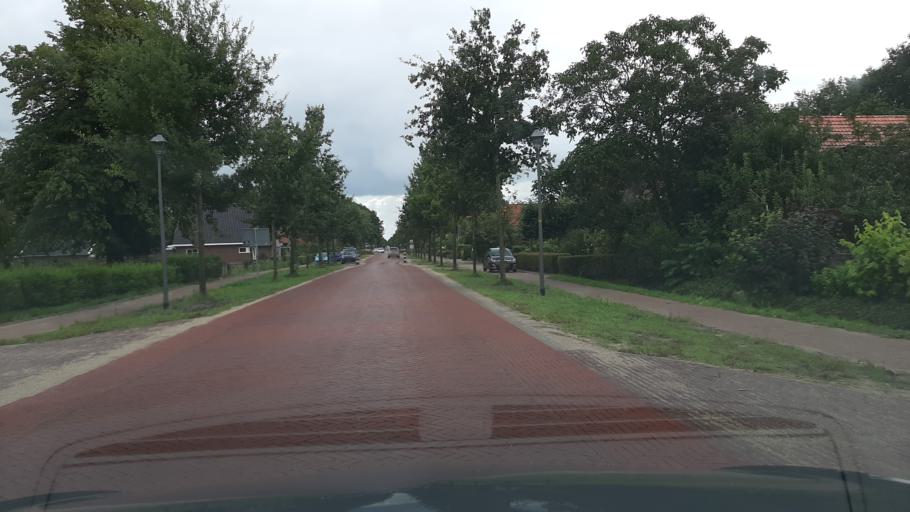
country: NL
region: Overijssel
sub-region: Gemeente Steenwijkerland
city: Steenwijkerwold
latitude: 52.8271
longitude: 6.0599
